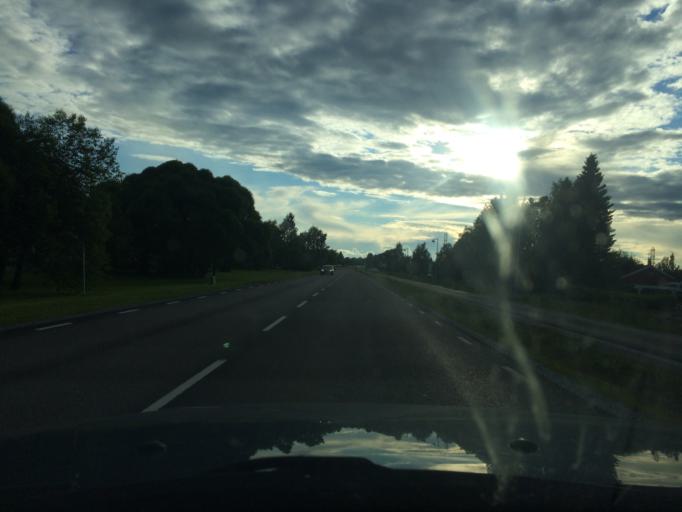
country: SE
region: Norrbotten
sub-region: Pitea Kommun
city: Pitea
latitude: 65.3233
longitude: 21.4580
